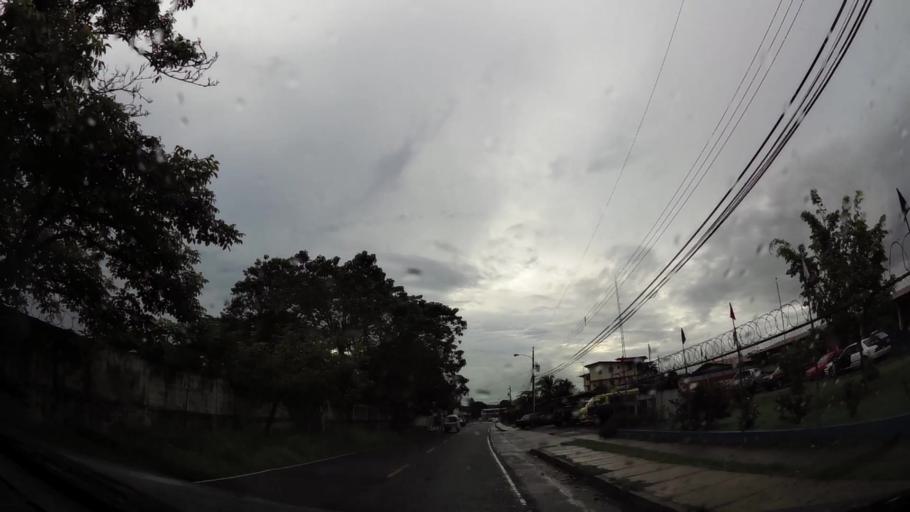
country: PA
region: Veraguas
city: Santiago de Veraguas
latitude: 8.1003
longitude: -80.9742
